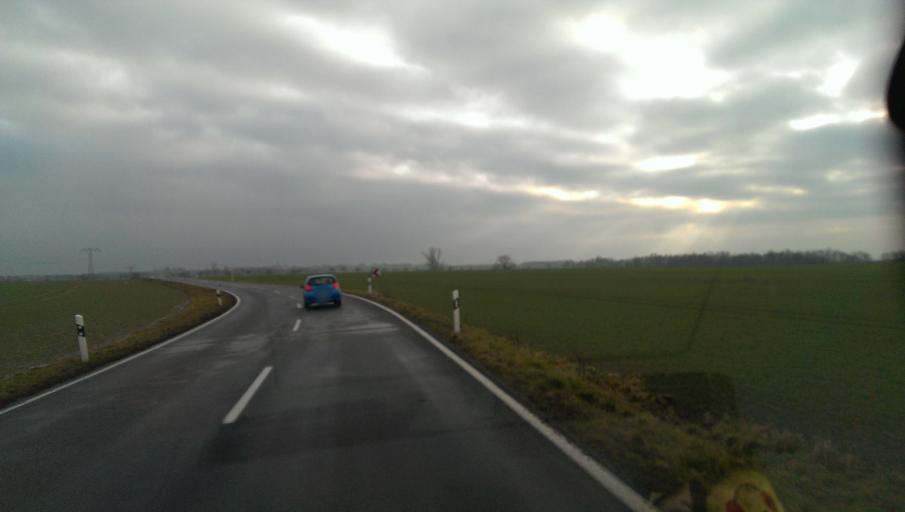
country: DE
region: Saxony
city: Priestewitz
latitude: 51.2343
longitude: 13.5561
